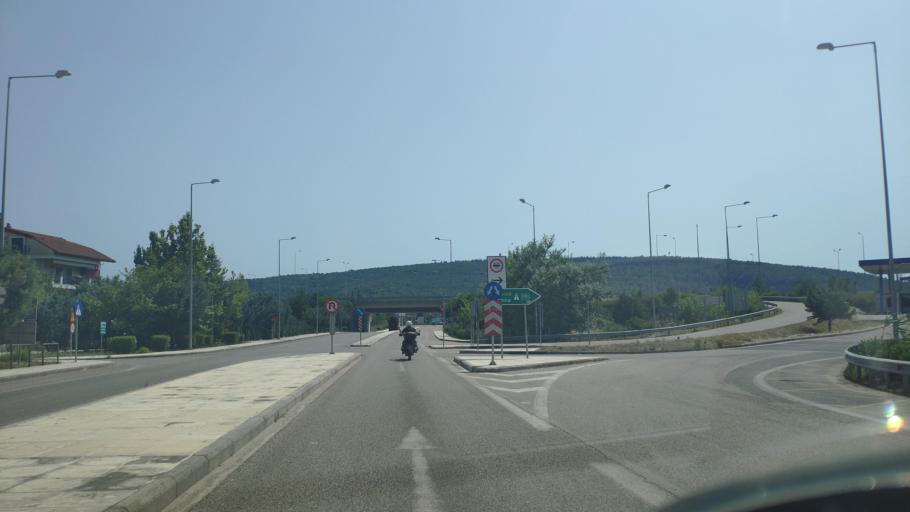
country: GR
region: Epirus
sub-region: Nomos Artas
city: Peta
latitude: 39.1611
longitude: 21.0132
